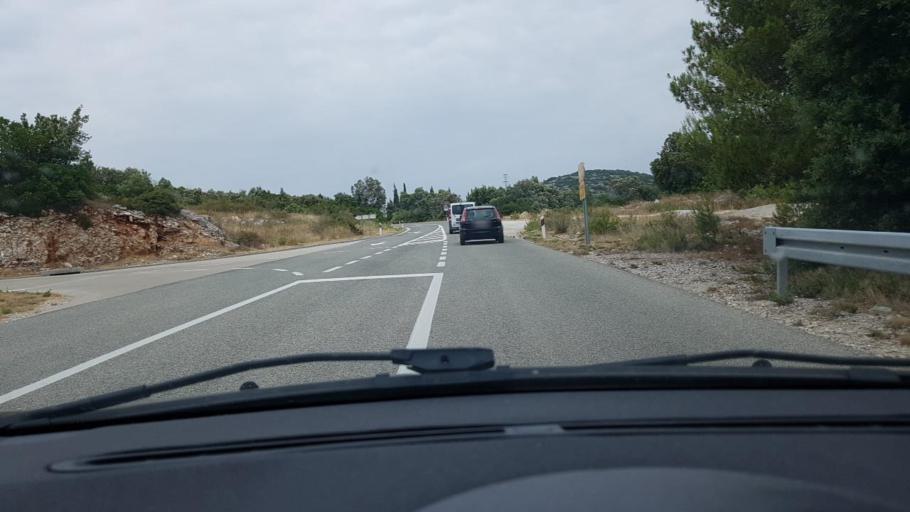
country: HR
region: Dubrovacko-Neretvanska
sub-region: Grad Korcula
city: Zrnovo
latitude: 42.9423
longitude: 17.0532
